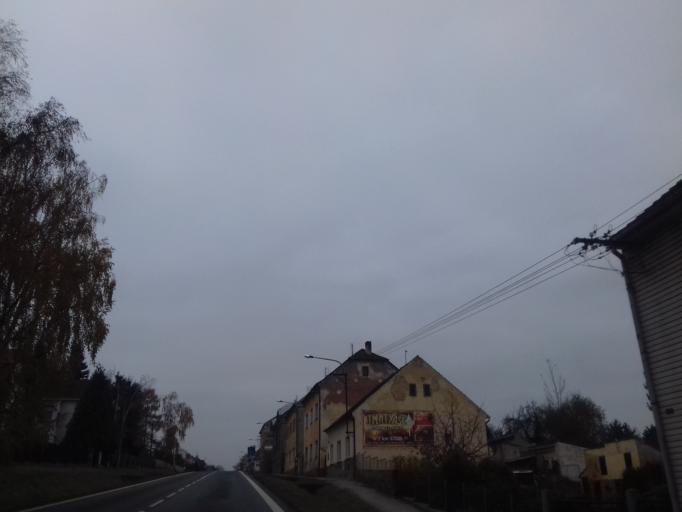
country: CZ
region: Plzensky
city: Zbuch
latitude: 49.6797
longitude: 13.2277
